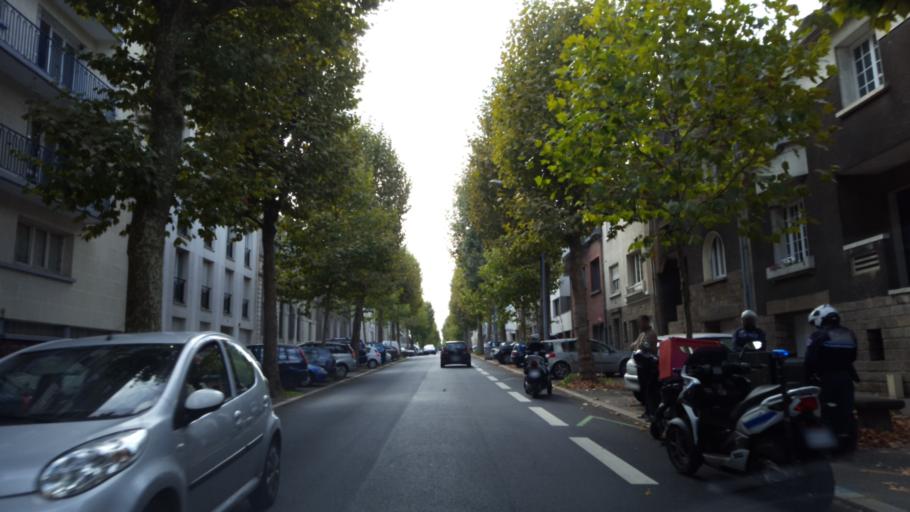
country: FR
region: Pays de la Loire
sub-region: Departement de la Loire-Atlantique
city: Nantes
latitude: 47.2096
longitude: -1.5775
